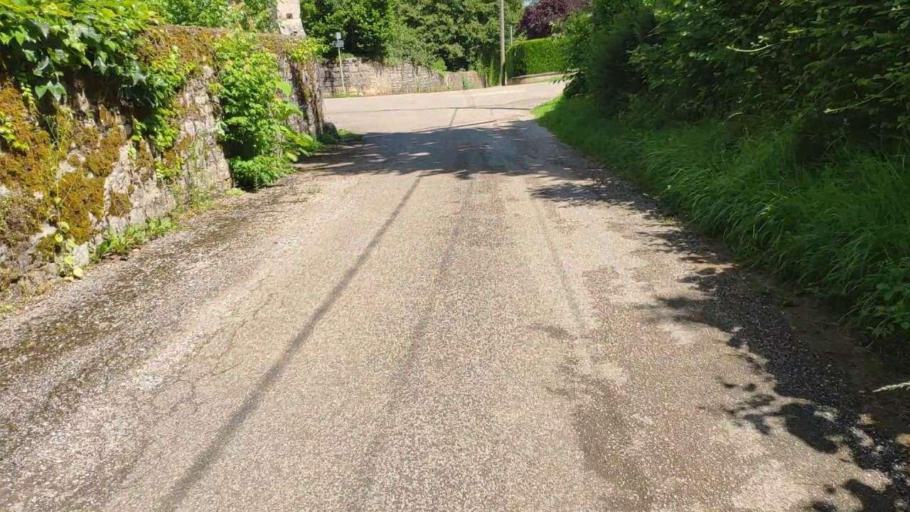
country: FR
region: Franche-Comte
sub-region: Departement du Jura
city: Bletterans
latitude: 46.8258
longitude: 5.5661
